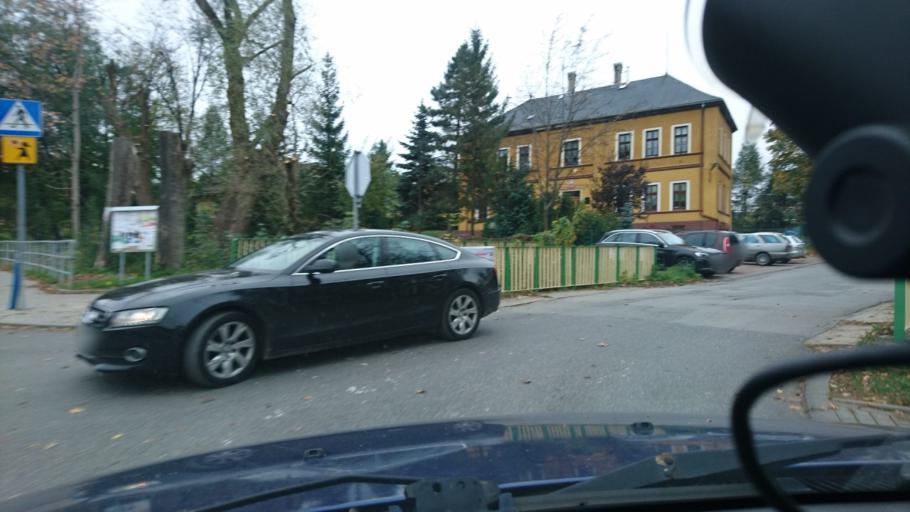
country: PL
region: Silesian Voivodeship
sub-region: Bielsko-Biala
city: Bielsko-Biala
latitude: 49.7934
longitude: 19.0125
